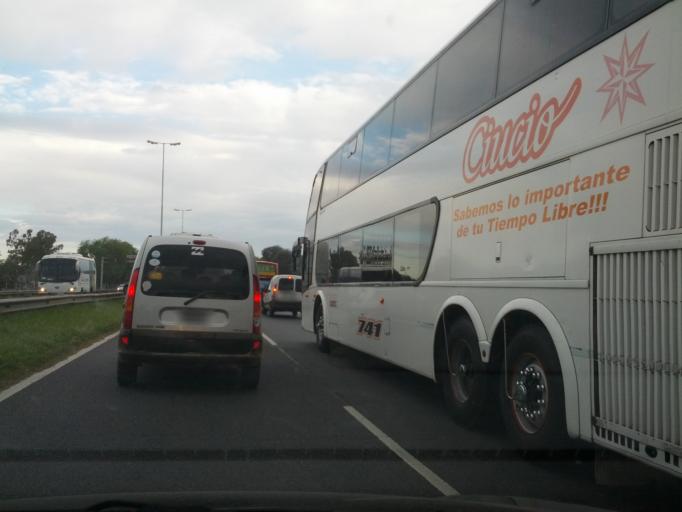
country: AR
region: Buenos Aires
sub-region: Partido de General Rodriguez
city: General Rodriguez
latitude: -34.6033
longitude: -58.8964
